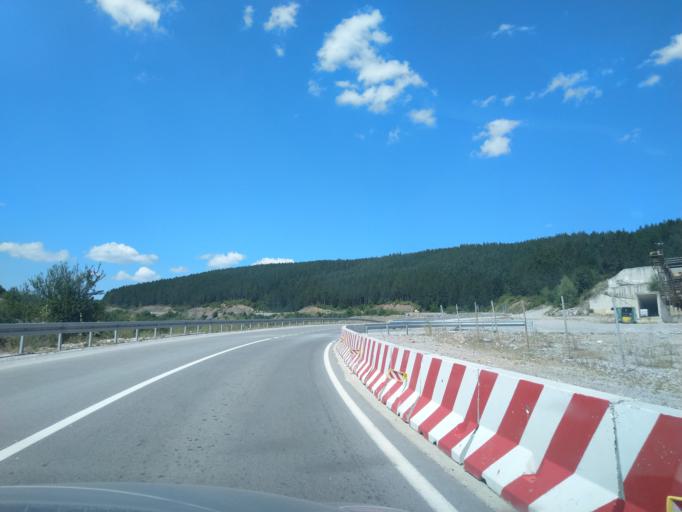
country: RS
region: Central Serbia
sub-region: Zlatiborski Okrug
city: Sjenica
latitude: 43.2965
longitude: 19.9365
